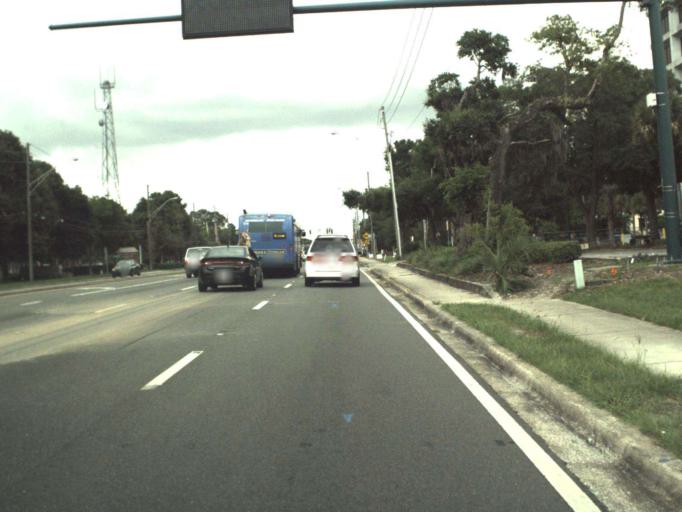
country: US
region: Florida
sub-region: Seminole County
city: Altamonte Springs
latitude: 28.6630
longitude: -81.3620
